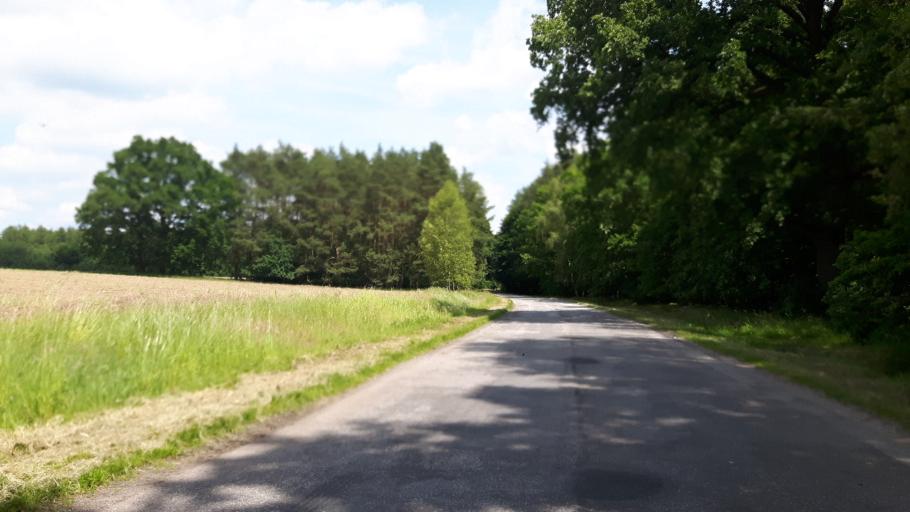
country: PL
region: West Pomeranian Voivodeship
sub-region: Powiat goleniowski
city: Osina
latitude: 53.6511
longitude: 14.9566
